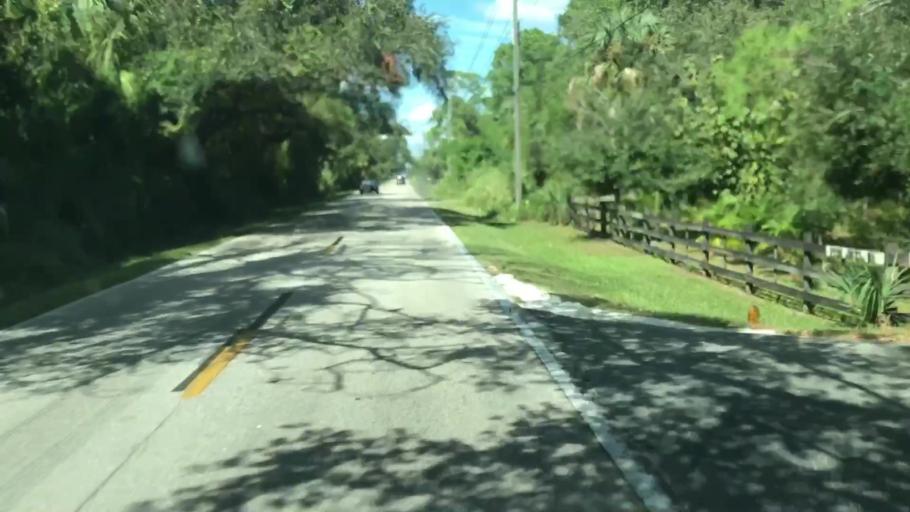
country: US
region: Florida
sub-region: Lee County
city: Alva
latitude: 26.6990
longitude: -81.6008
